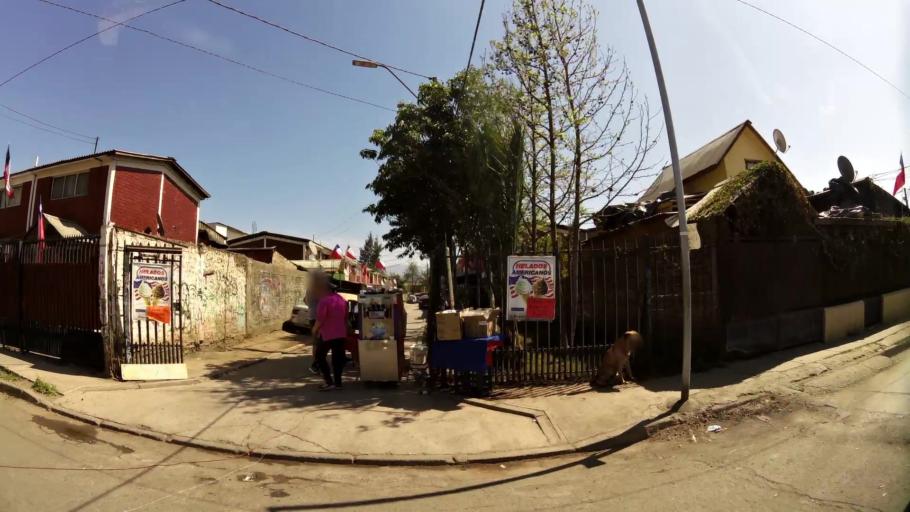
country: CL
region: Santiago Metropolitan
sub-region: Provincia de Santiago
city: Lo Prado
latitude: -33.4108
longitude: -70.7408
